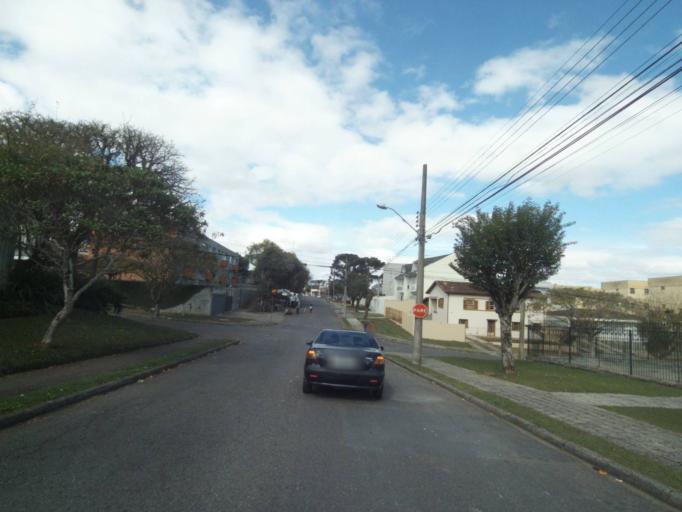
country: BR
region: Parana
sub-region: Curitiba
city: Curitiba
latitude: -25.4593
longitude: -49.2751
